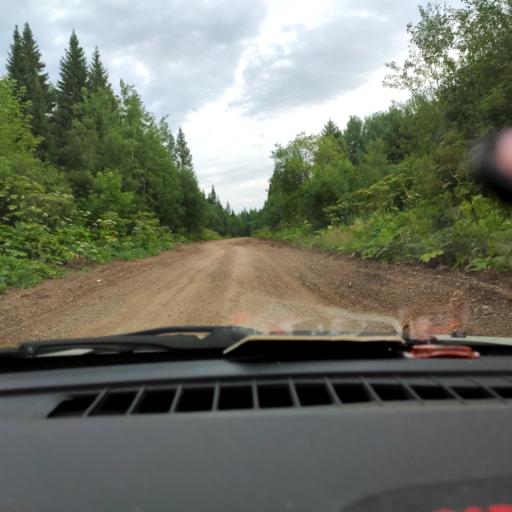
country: RU
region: Perm
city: Kultayevo
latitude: 57.8140
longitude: 56.0017
